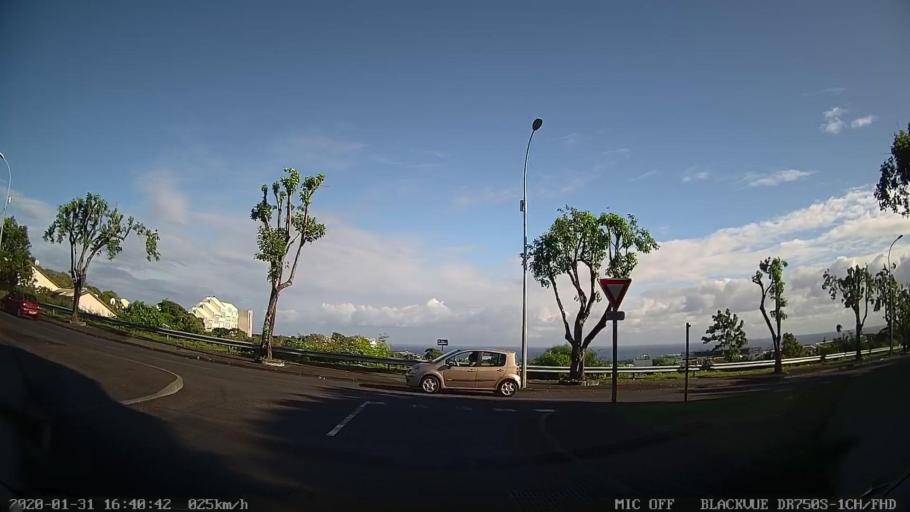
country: RE
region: Reunion
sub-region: Reunion
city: Saint-Denis
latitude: -20.9062
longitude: 55.4858
